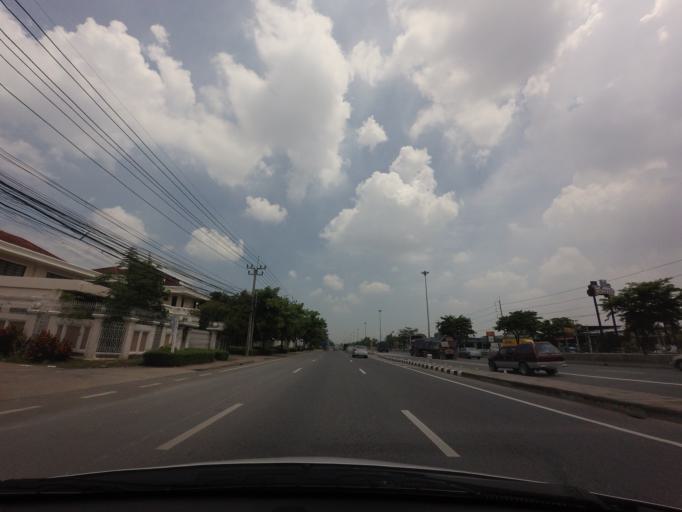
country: TH
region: Bangkok
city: Taling Chan
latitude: 13.7739
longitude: 100.4084
